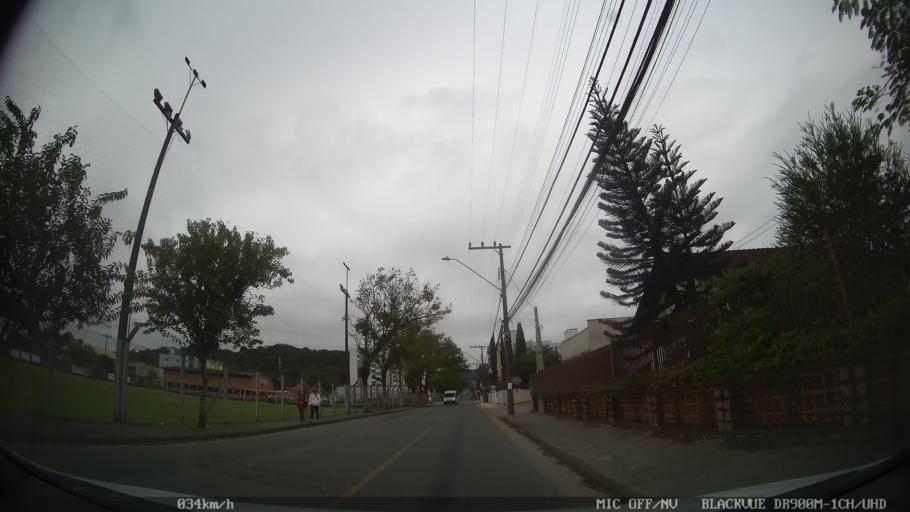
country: BR
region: Santa Catarina
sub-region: Joinville
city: Joinville
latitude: -26.2656
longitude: -48.8576
